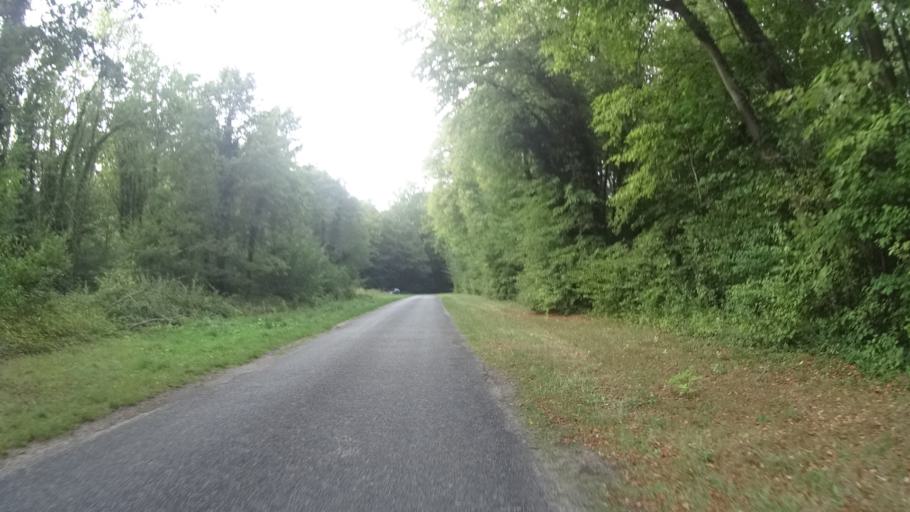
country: FR
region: Picardie
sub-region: Departement de l'Oise
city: Ver-sur-Launette
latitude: 49.1632
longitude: 2.6795
